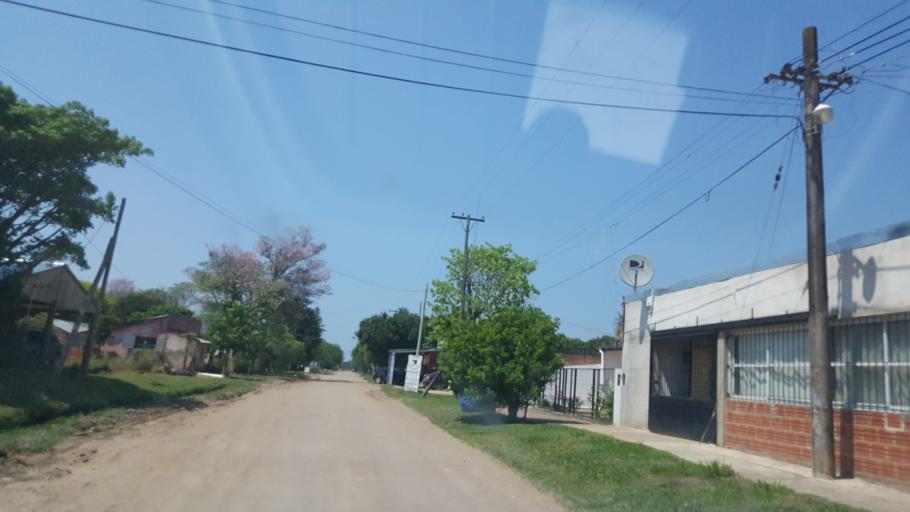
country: AR
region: Corrientes
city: Ita Ibate
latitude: -27.4251
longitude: -57.3333
